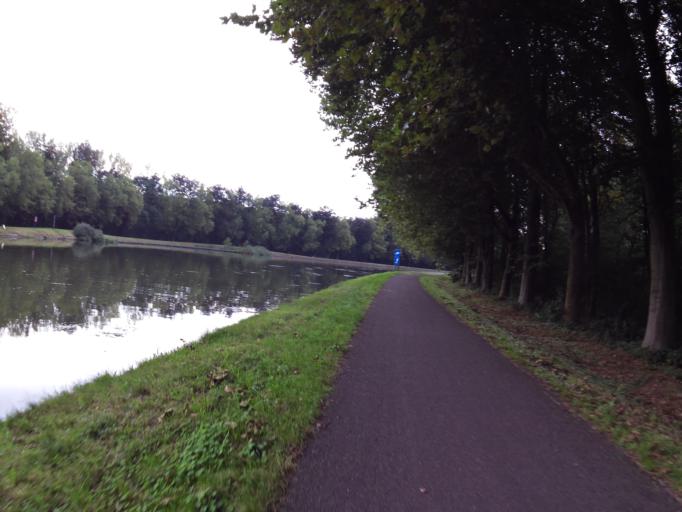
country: BE
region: Flanders
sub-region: Provincie Limburg
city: Kinrooi
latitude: 51.0720
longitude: 5.6977
